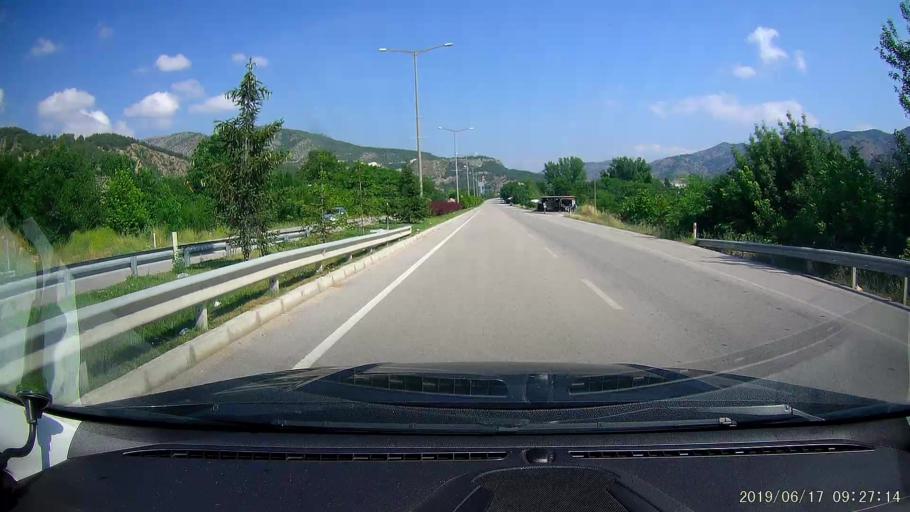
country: TR
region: Amasya
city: Amasya
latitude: 40.6751
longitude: 35.8281
